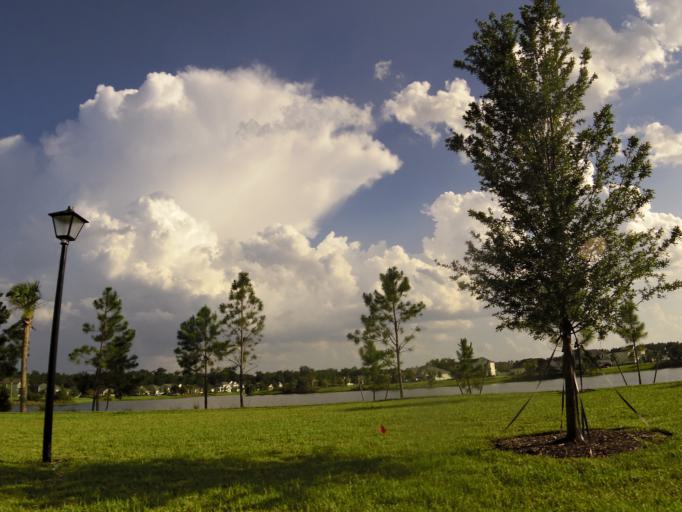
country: US
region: Florida
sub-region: Clay County
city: Green Cove Springs
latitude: 30.0300
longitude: -81.6311
